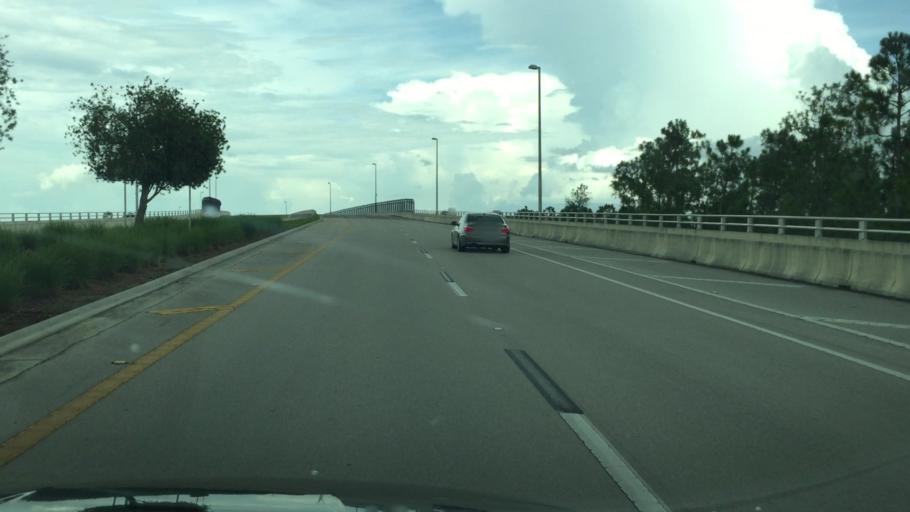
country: US
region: Florida
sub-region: Lee County
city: Three Oaks
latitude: 26.4491
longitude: -81.7864
